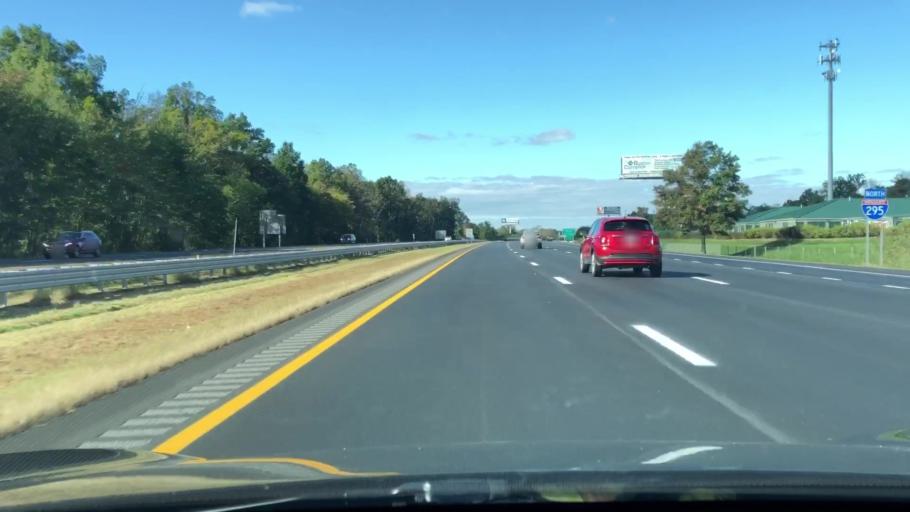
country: US
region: New Jersey
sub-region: Mercer County
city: Ewing
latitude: 40.2898
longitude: -74.7915
